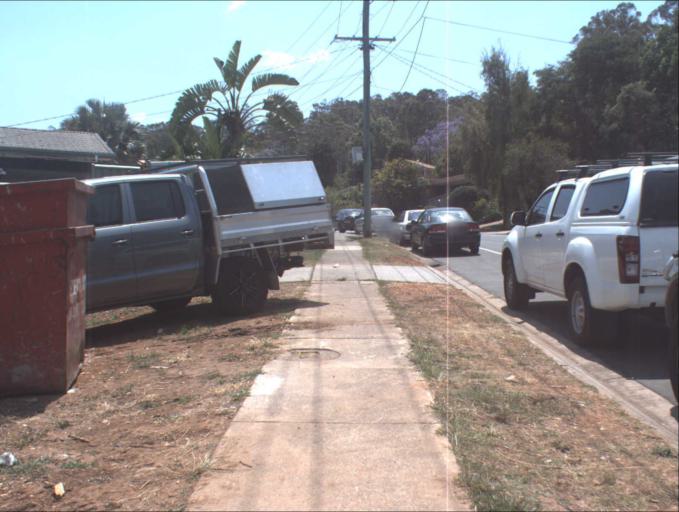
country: AU
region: Queensland
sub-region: Logan
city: Slacks Creek
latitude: -27.6647
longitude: 153.1919
